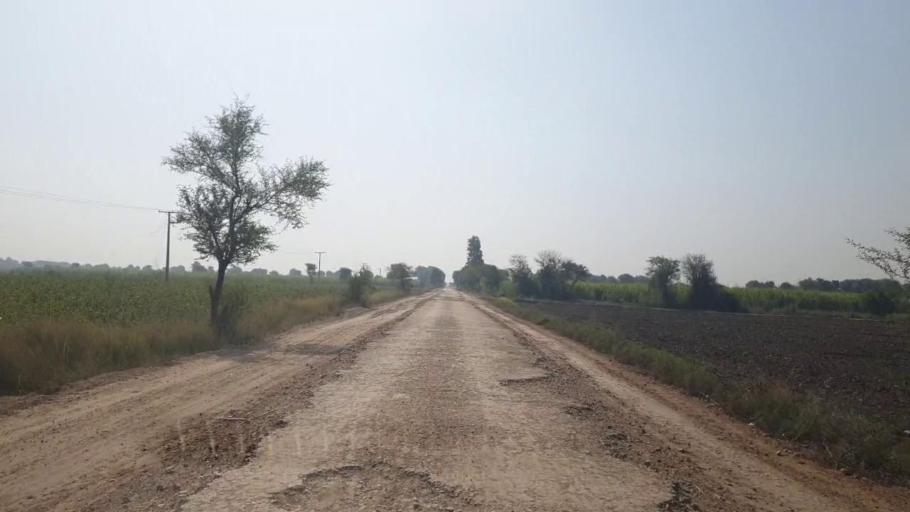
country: PK
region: Sindh
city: Shahdadpur
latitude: 25.9114
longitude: 68.7412
